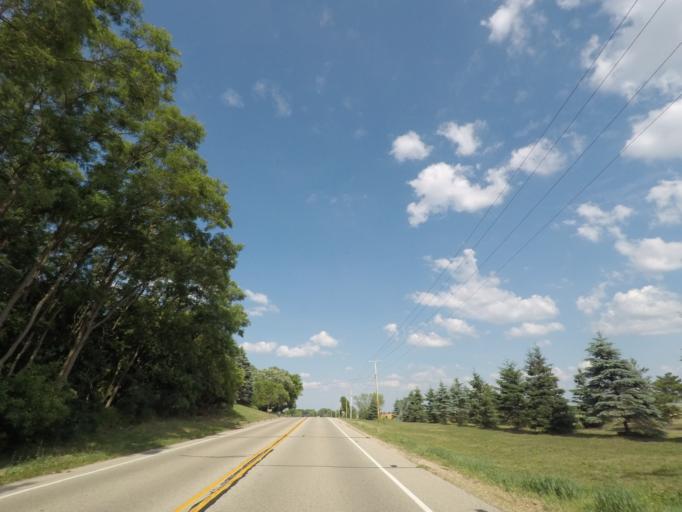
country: US
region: Wisconsin
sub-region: Walworth County
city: East Troy
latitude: 42.7931
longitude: -88.4873
